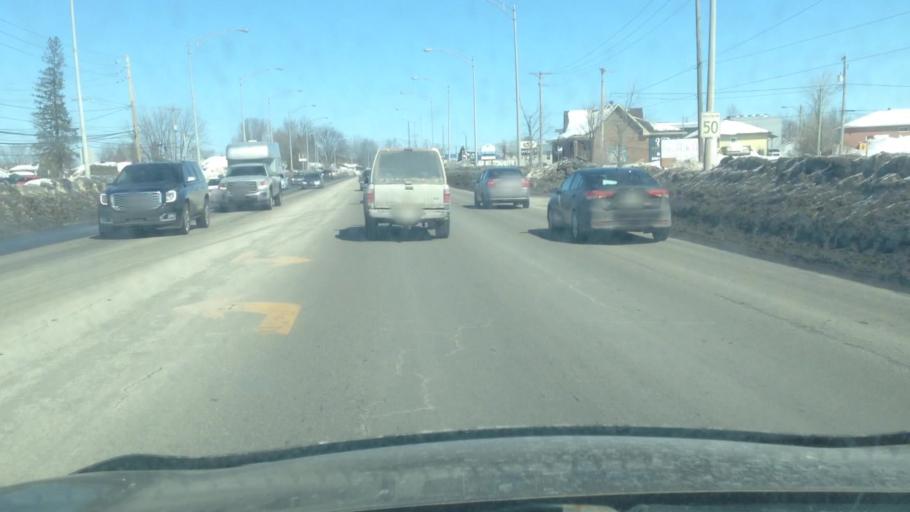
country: CA
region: Quebec
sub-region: Laurentides
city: Saint-Jerome
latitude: 45.7561
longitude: -73.9961
